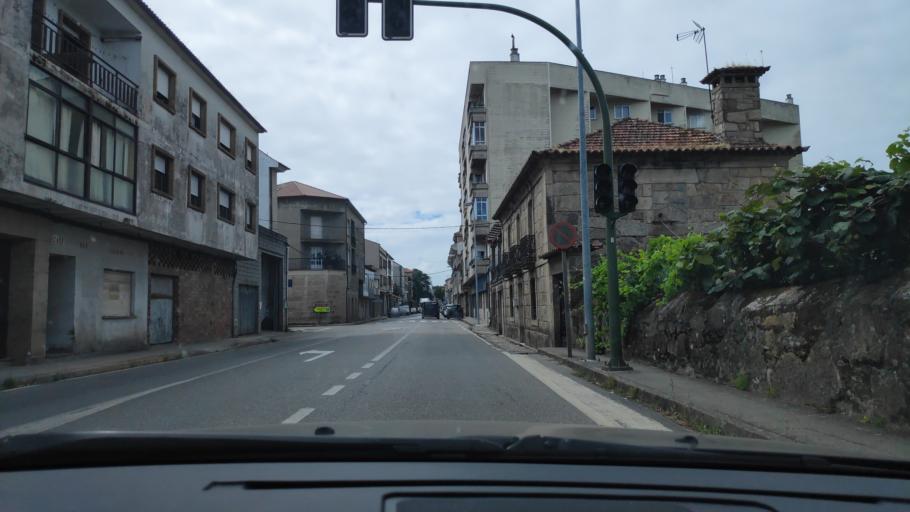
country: ES
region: Galicia
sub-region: Provincia de Pontevedra
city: Cambados
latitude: 42.5229
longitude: -8.8126
